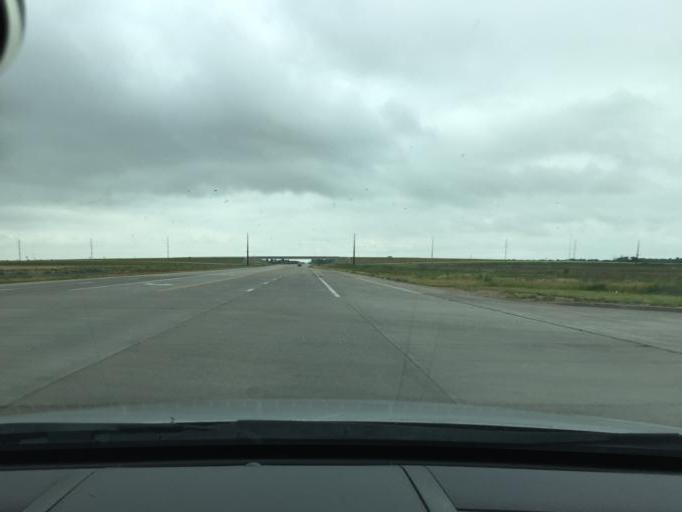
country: US
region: Kansas
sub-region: Reno County
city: Hutchinson
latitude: 38.0341
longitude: -97.8671
